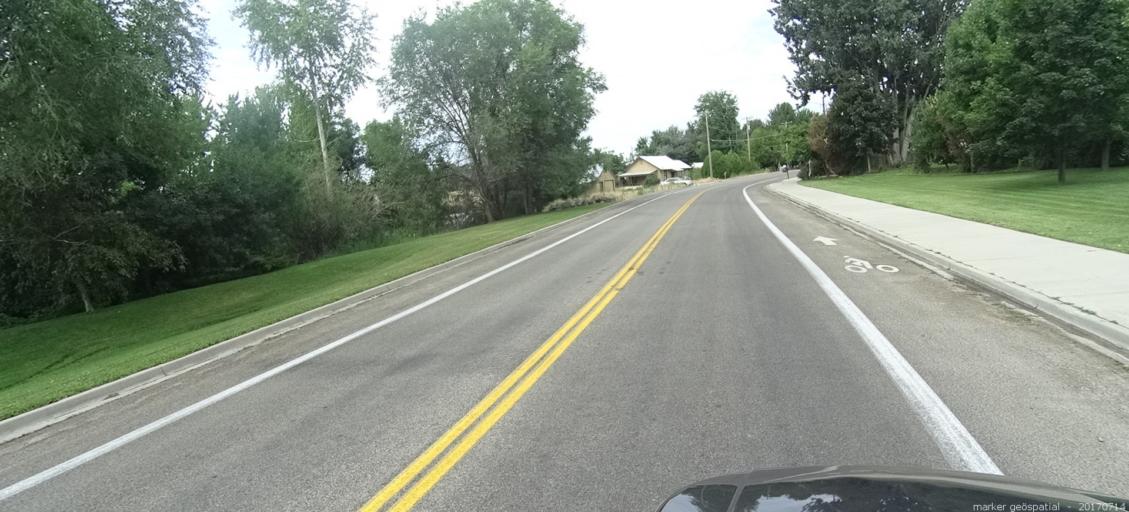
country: US
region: Idaho
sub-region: Ada County
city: Kuna
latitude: 43.4923
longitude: -116.4292
